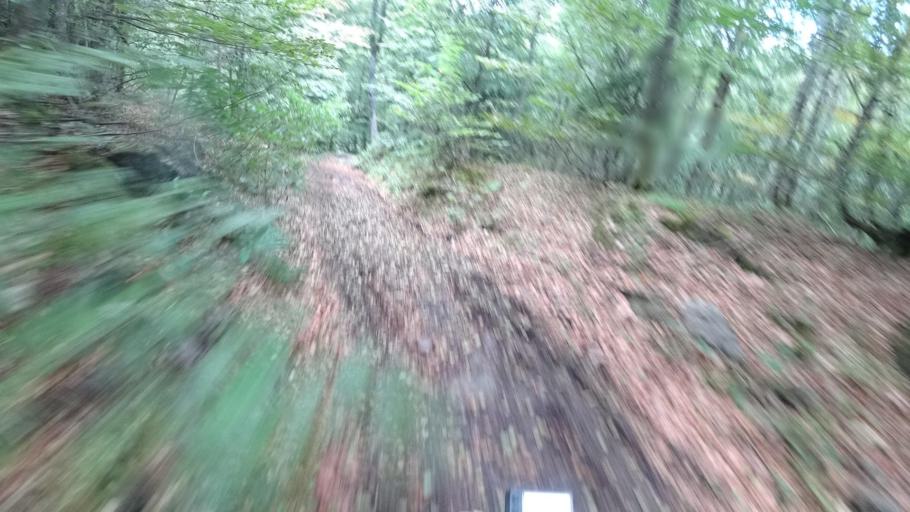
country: HR
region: Karlovacka
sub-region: Grad Ogulin
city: Ogulin
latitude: 45.2291
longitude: 15.1830
